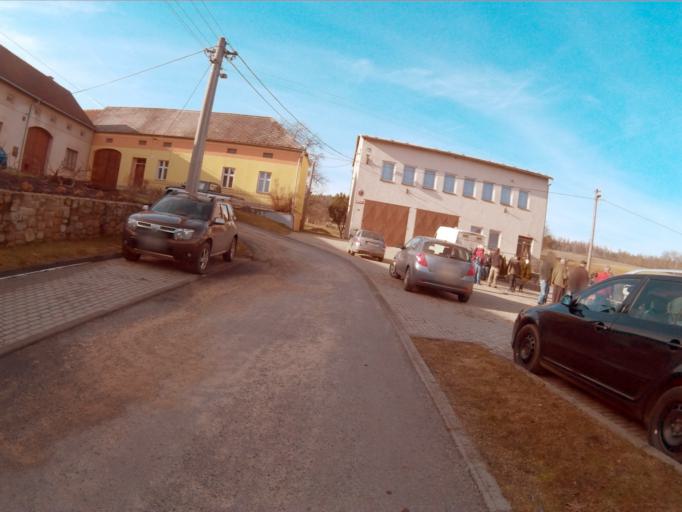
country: CZ
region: Vysocina
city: Mohelno
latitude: 49.1455
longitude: 16.1704
